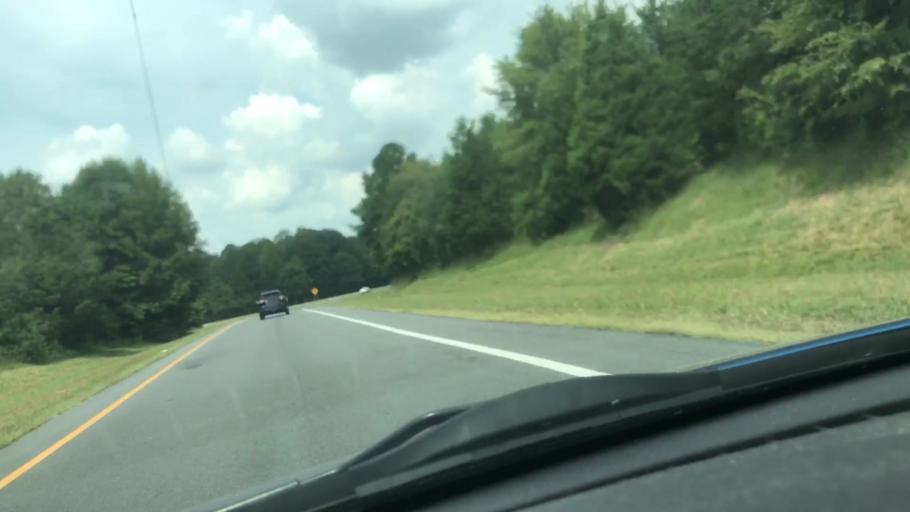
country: US
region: North Carolina
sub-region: Randolph County
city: Randleman
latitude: 35.8267
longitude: -79.8251
